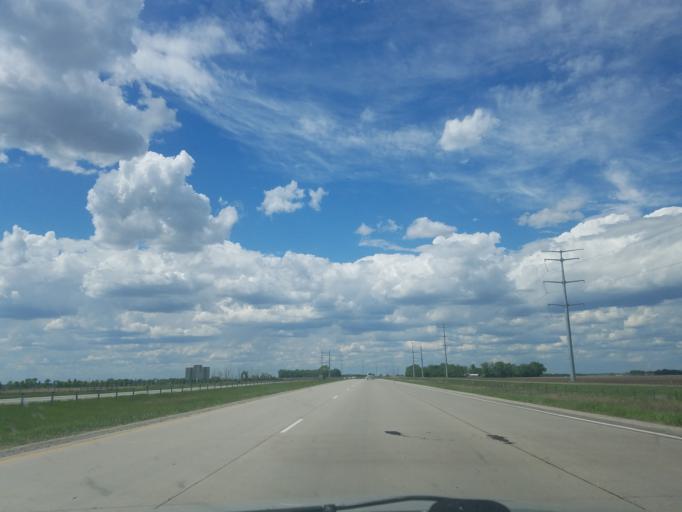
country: US
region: Minnesota
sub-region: Clay County
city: Barnesville
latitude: 46.5618
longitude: -96.3181
